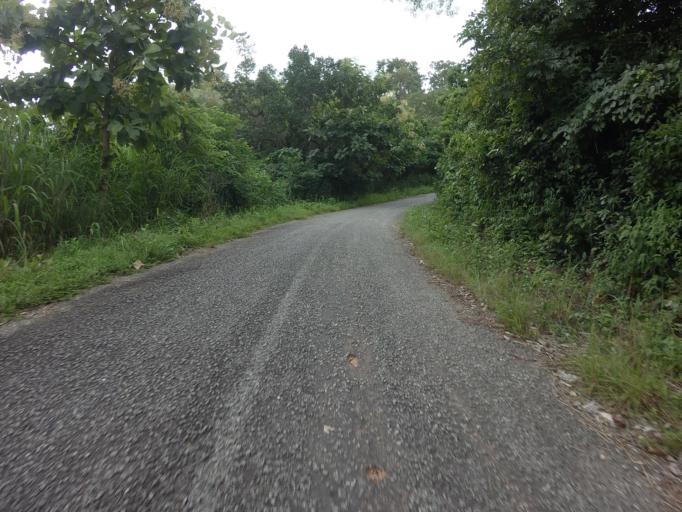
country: GH
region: Volta
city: Kpandu
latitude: 6.8828
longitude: 0.4438
